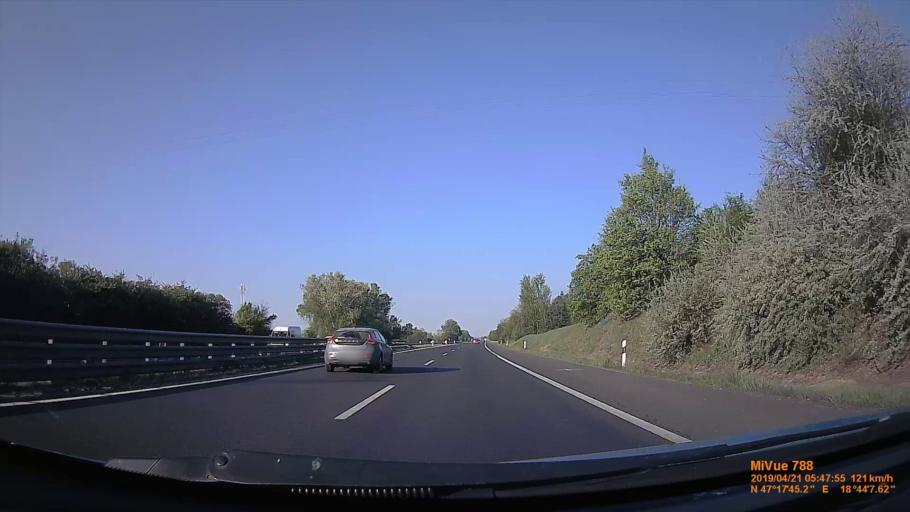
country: HU
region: Fejer
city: Baracska
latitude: 47.2942
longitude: 18.7348
